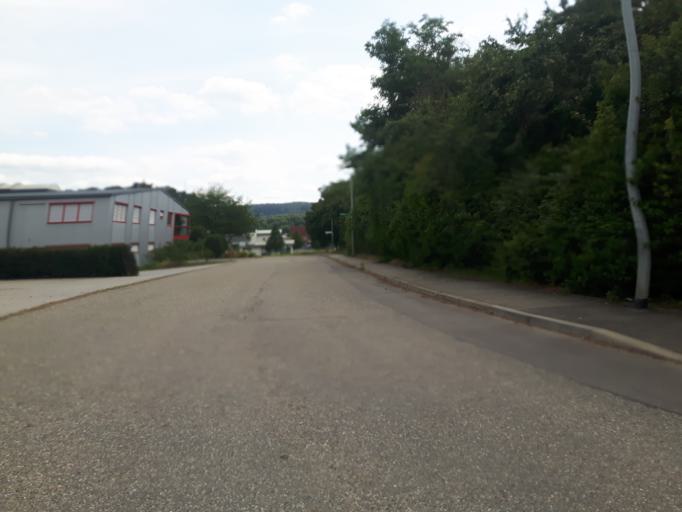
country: DE
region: Baden-Wuerttemberg
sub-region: Regierungsbezirk Stuttgart
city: Zaberfeld
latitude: 49.0642
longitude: 8.9301
